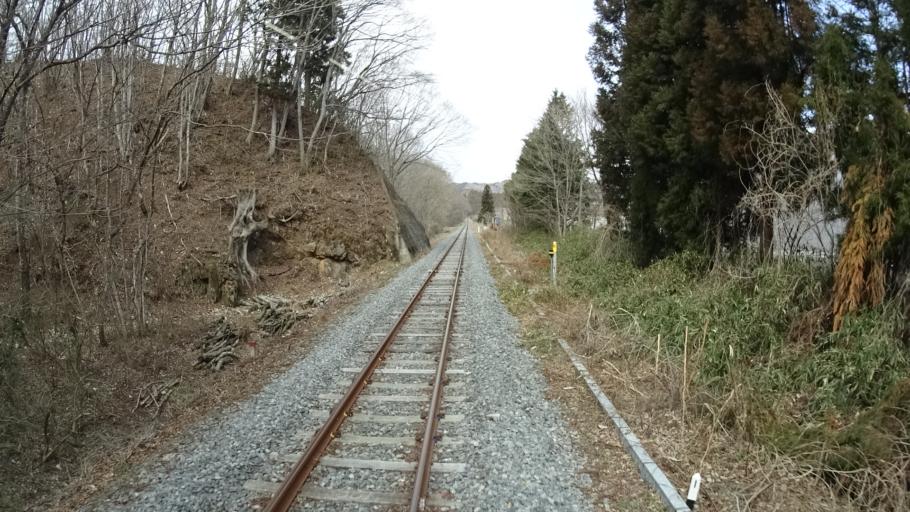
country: JP
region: Iwate
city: Miyako
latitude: 39.5575
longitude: 141.9393
